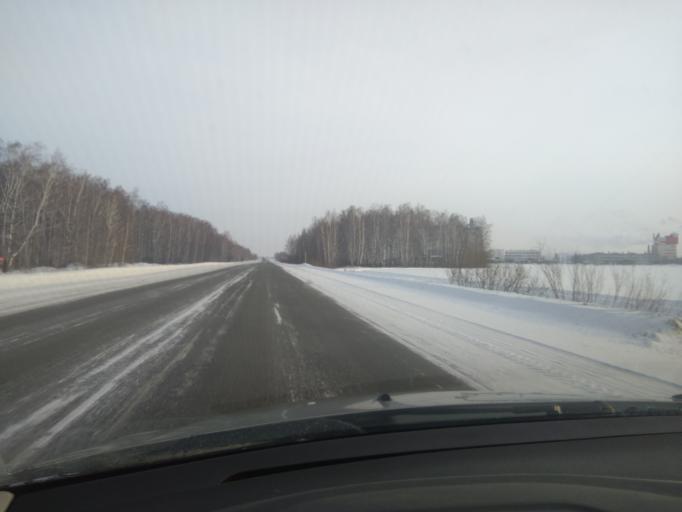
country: RU
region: Sverdlovsk
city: Bogdanovich
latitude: 56.8041
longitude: 62.0258
